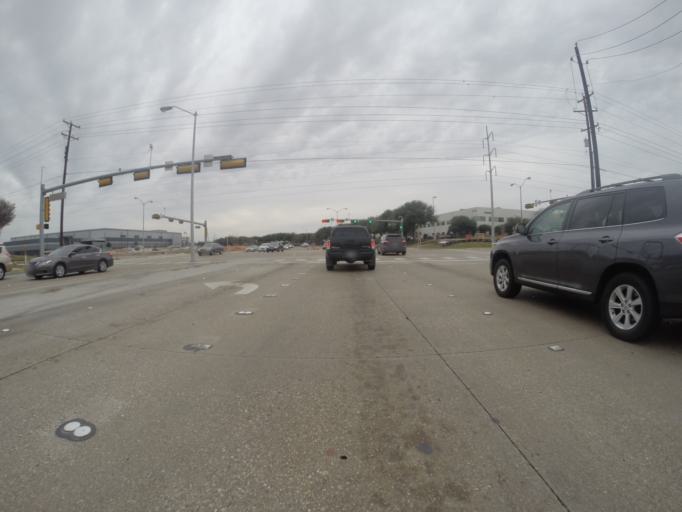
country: US
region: Texas
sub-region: Collin County
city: Saint Paul
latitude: 33.0289
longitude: -96.5612
